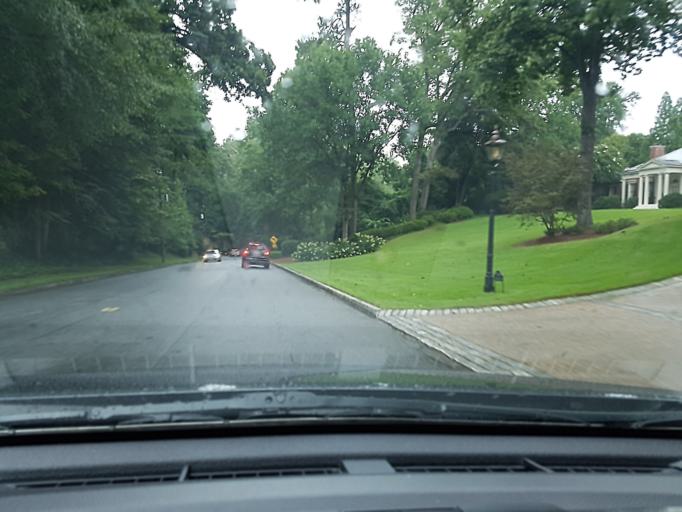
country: US
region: Georgia
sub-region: DeKalb County
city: North Atlanta
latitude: 33.8351
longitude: -84.3887
